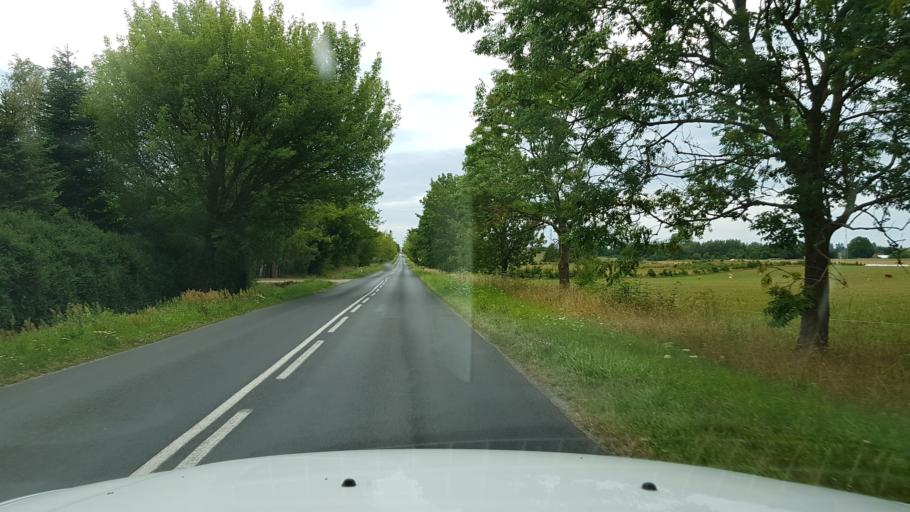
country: PL
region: West Pomeranian Voivodeship
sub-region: Powiat kolobrzeski
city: Kolobrzeg
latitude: 54.1466
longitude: 15.6444
